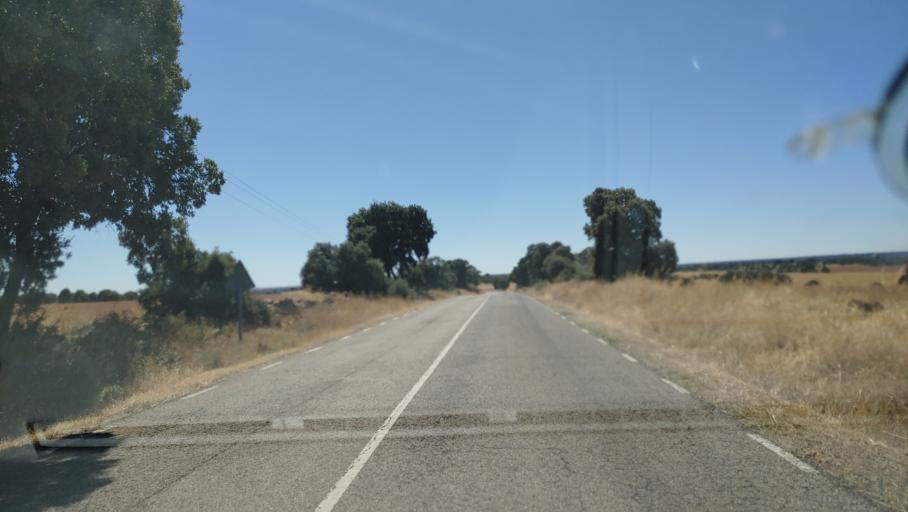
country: ES
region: Castille-La Mancha
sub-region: Provincia de Albacete
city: Ossa de Montiel
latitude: 38.9214
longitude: -2.7558
